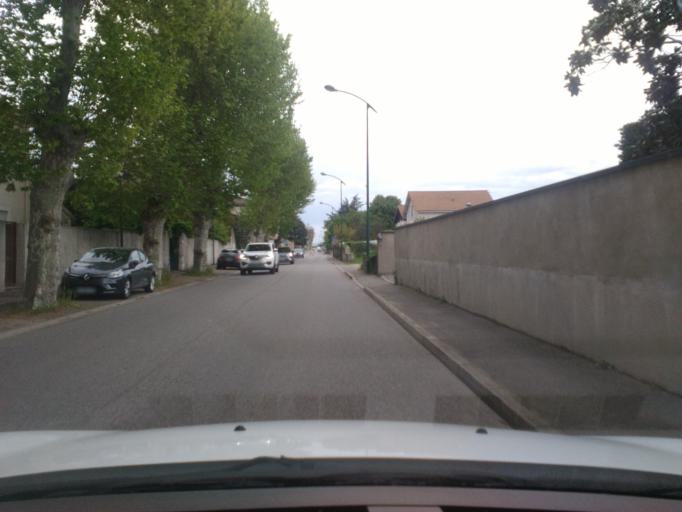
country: FR
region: Rhone-Alpes
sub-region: Departement de l'Ardeche
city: Cornas
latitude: 44.9627
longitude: 4.8486
